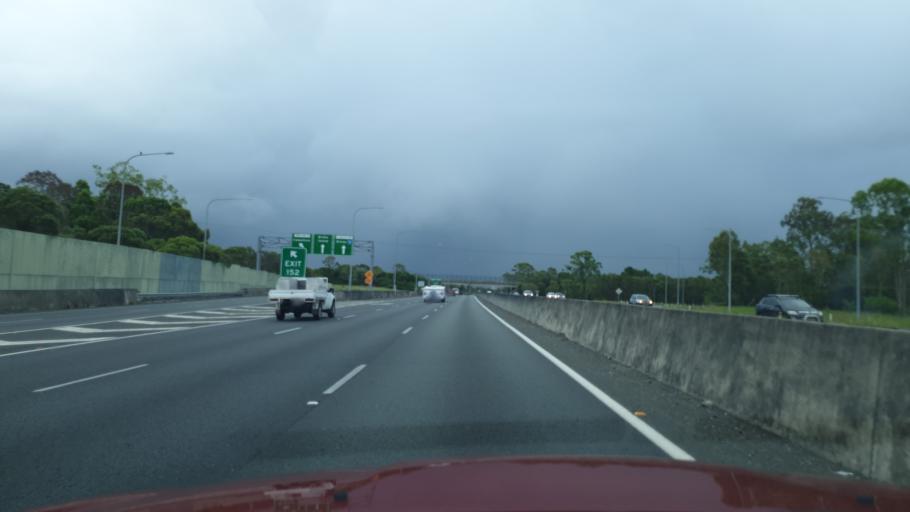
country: AU
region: Queensland
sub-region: Moreton Bay
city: Caboolture
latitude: -27.0891
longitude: 152.9754
